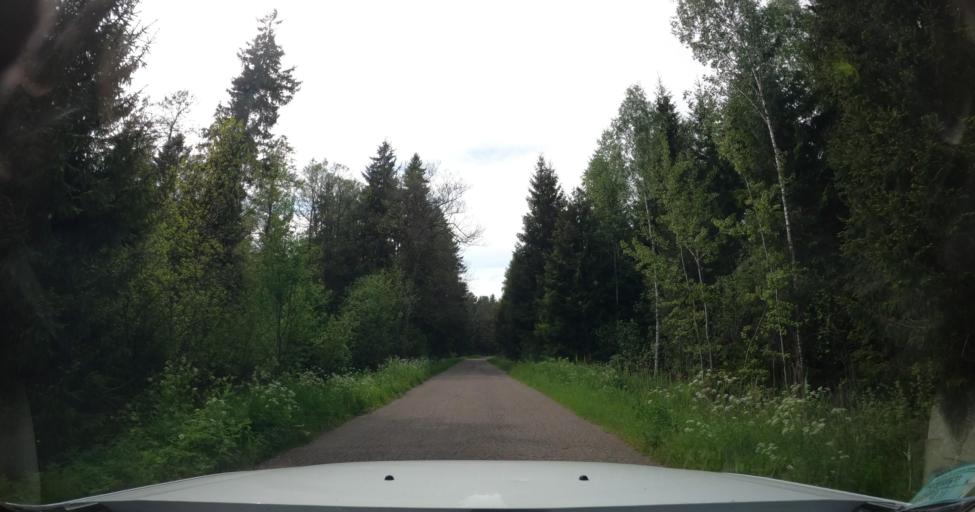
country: PL
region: Warmian-Masurian Voivodeship
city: Dobre Miasto
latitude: 54.0960
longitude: 20.3919
